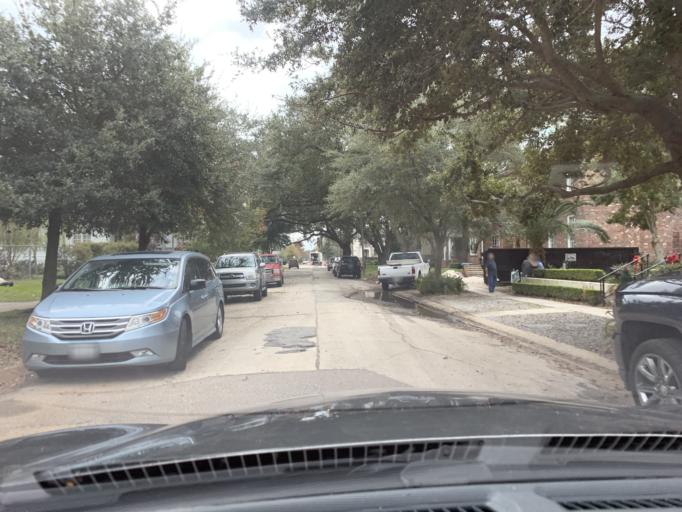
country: US
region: Louisiana
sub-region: Jefferson Parish
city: Metairie
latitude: 30.0149
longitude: -90.1035
